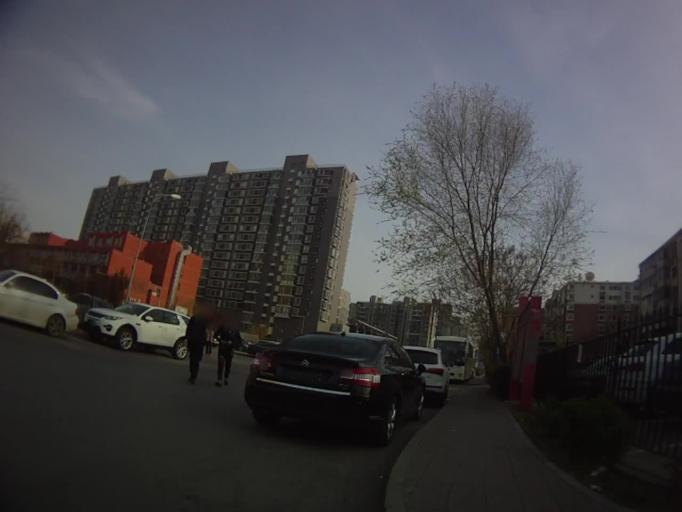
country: CN
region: Beijing
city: Longtan
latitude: 39.8980
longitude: 116.4439
